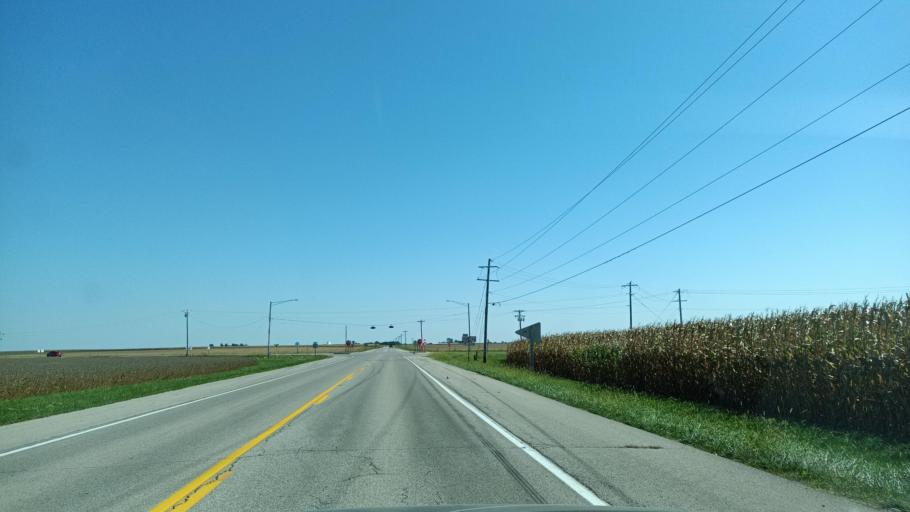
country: US
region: Illinois
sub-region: McLean County
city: Le Roy
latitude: 40.3124
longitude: -88.7017
